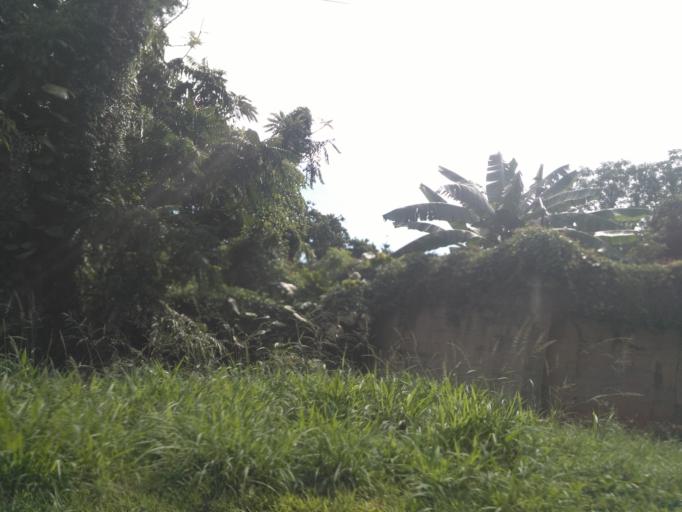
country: UG
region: Central Region
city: Kampala Central Division
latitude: 0.3278
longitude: 32.5806
